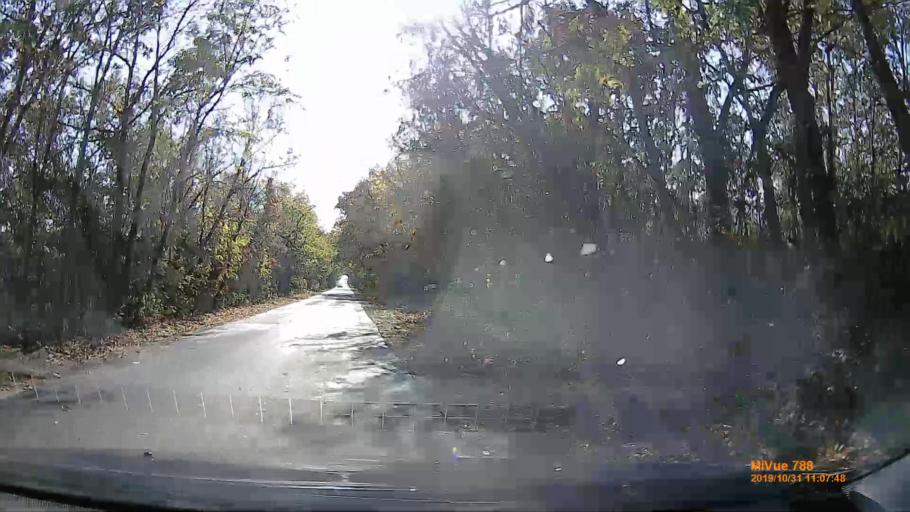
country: HU
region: Pest
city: Urom
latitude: 47.5937
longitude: 19.0018
